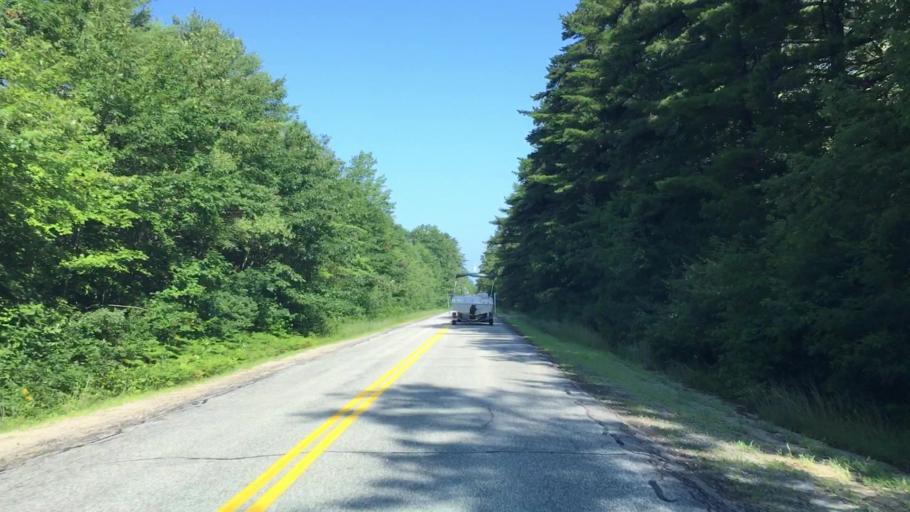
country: US
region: Maine
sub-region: Androscoggin County
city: Poland
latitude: 44.0476
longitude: -70.3635
